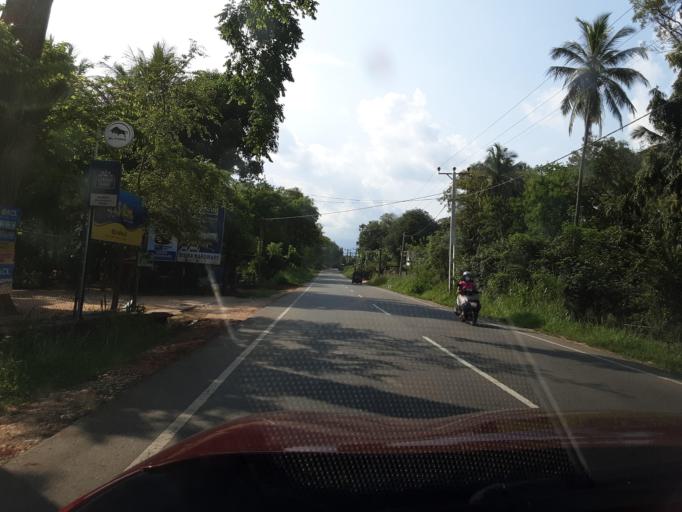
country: LK
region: Uva
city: Haputale
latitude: 6.6118
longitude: 81.1323
